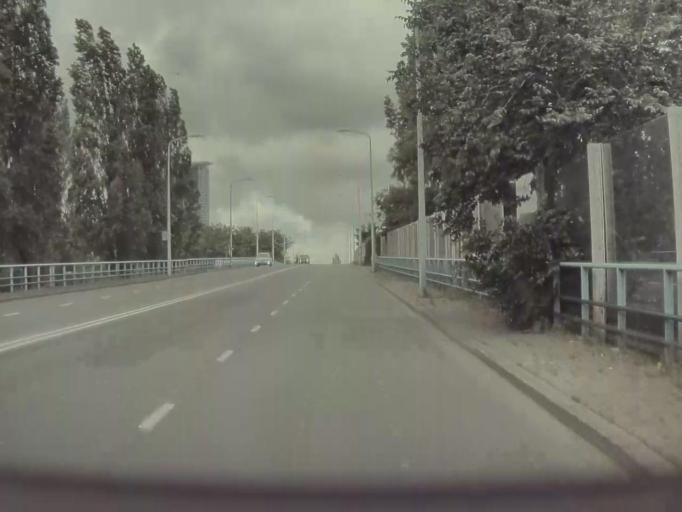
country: NL
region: South Holland
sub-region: Gemeente Leidschendam-Voorburg
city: Voorburg
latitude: 52.0783
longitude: 4.3325
